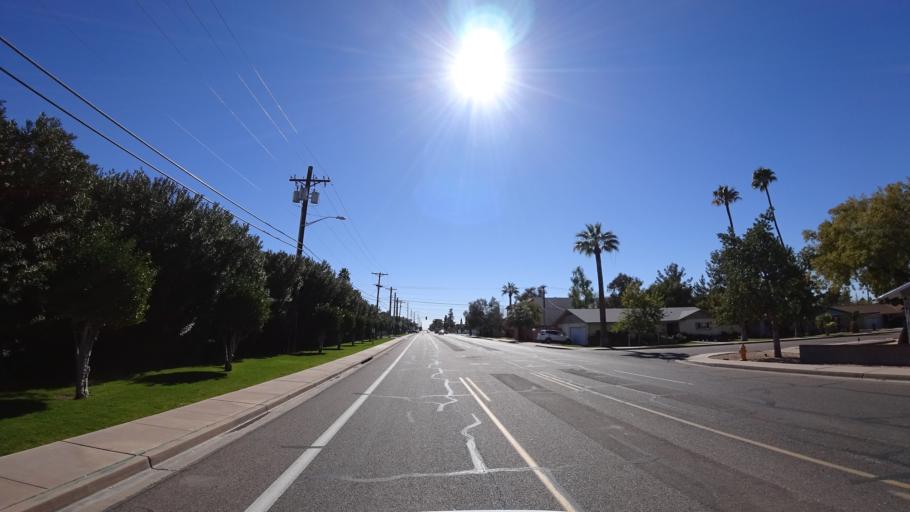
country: US
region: Arizona
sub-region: Maricopa County
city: Paradise Valley
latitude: 33.4815
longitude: -111.9695
